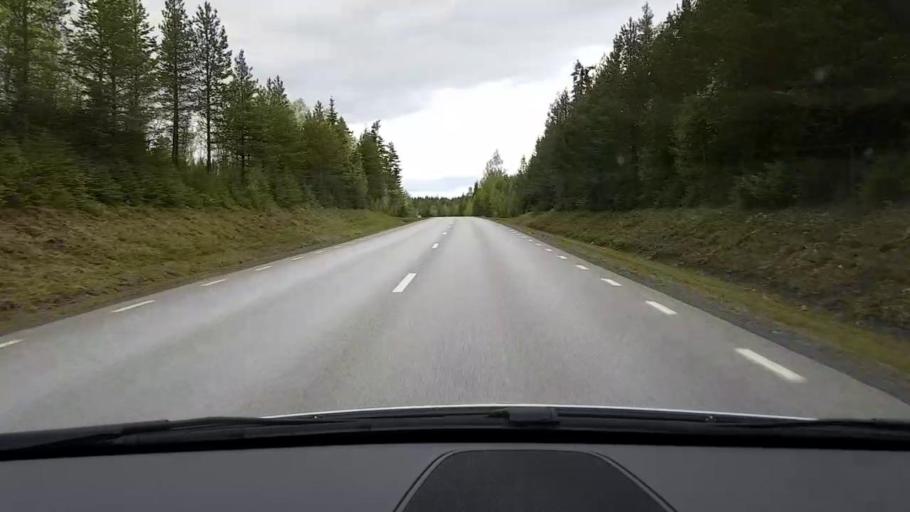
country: SE
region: Jaemtland
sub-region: Krokoms Kommun
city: Valla
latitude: 63.3006
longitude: 13.9262
